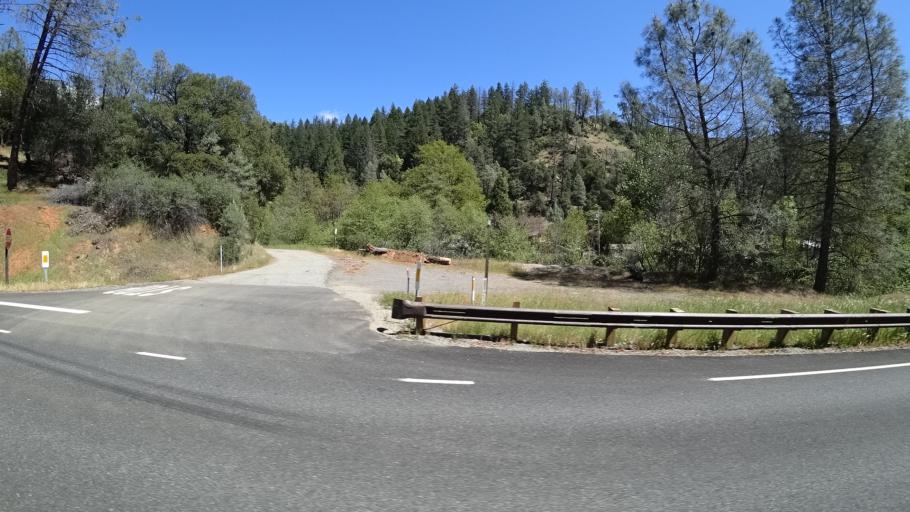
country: US
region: California
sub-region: Trinity County
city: Weaverville
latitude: 40.7323
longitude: -123.0542
